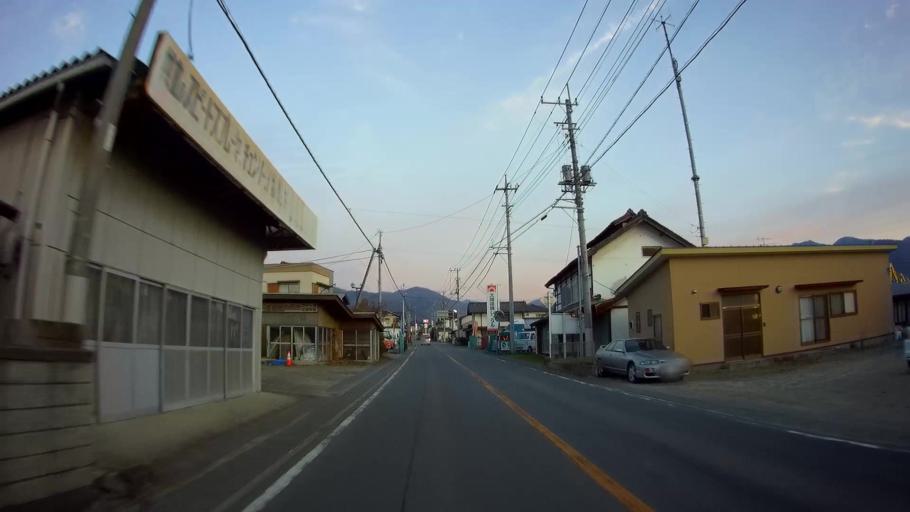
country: JP
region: Yamanashi
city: Enzan
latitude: 35.6645
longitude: 138.7016
